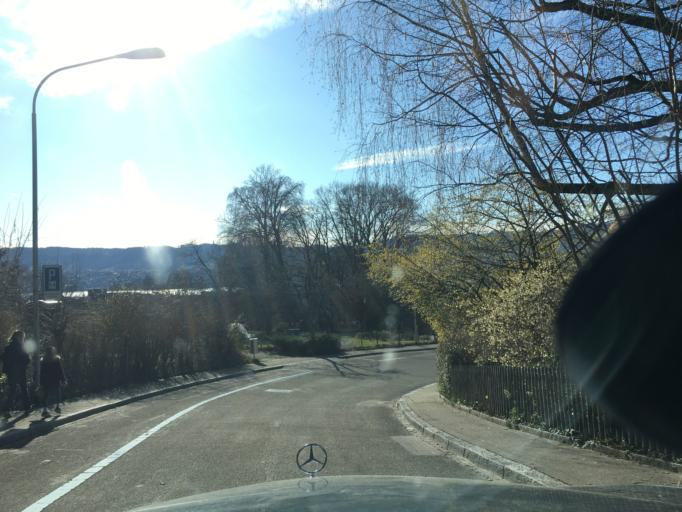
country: CH
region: Zurich
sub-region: Bezirk Zuerich
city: Zuerich (Kreis 7) / Witikon
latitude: 47.3553
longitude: 8.5811
